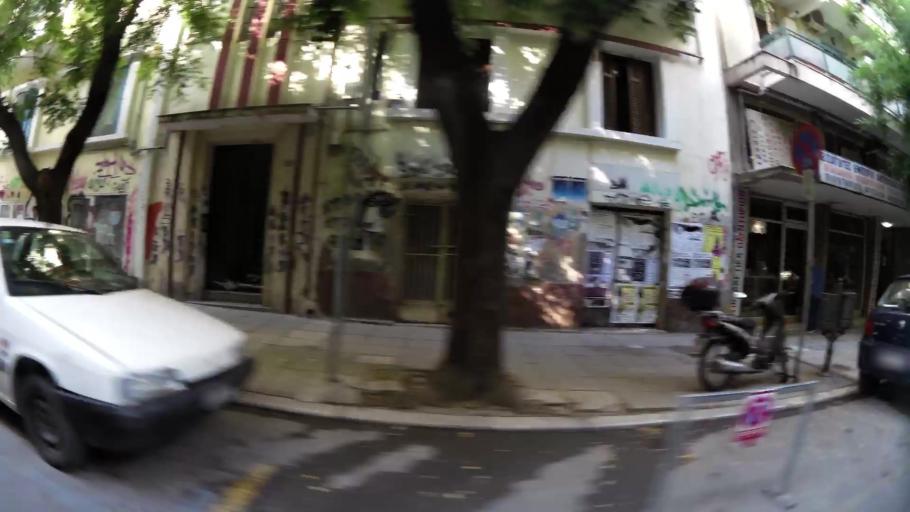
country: GR
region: Central Macedonia
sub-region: Nomos Thessalonikis
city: Sykies
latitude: 40.6372
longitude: 22.9482
